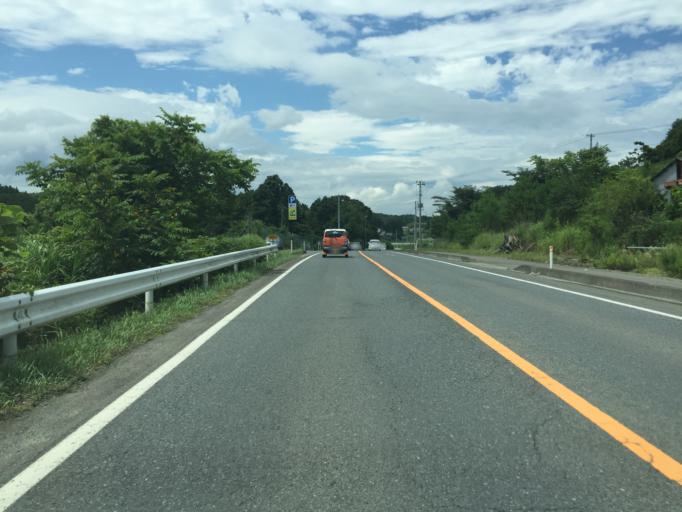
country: JP
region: Fukushima
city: Namie
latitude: 37.7235
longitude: 140.9544
